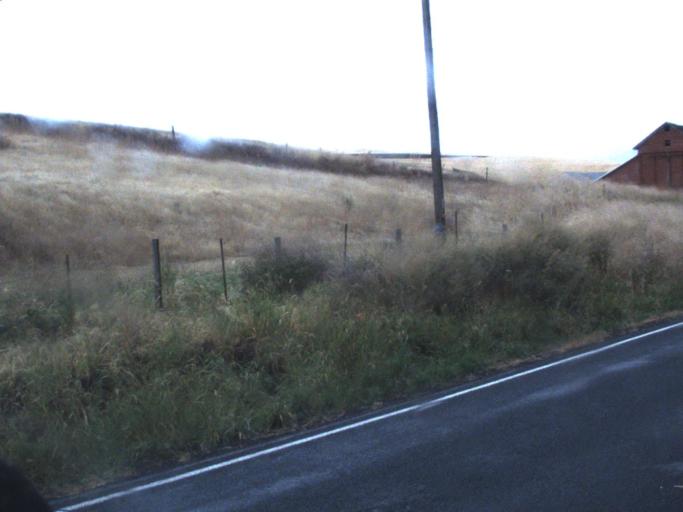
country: US
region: Washington
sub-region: Whitman County
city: Colfax
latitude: 47.0451
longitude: -117.5148
